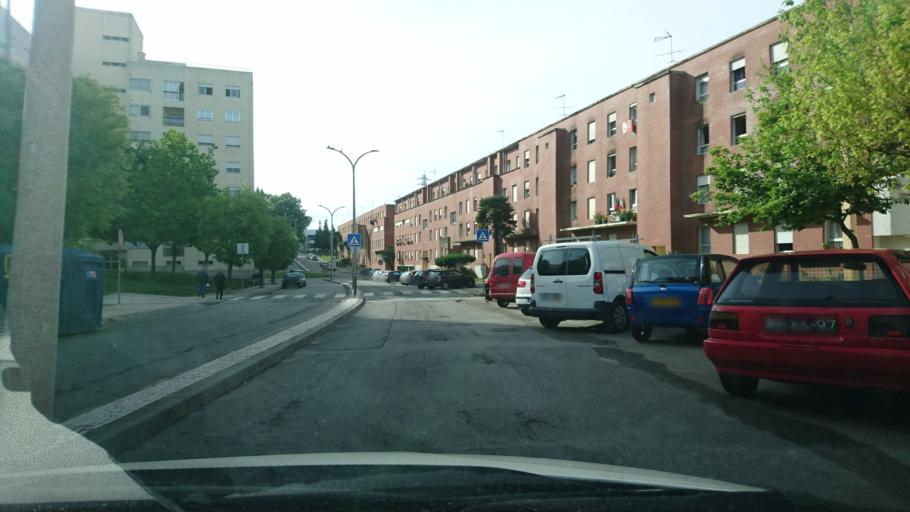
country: PT
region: Aveiro
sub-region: Sao Joao da Madeira
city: Sao Joao da Madeira
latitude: 40.8886
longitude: -8.4931
